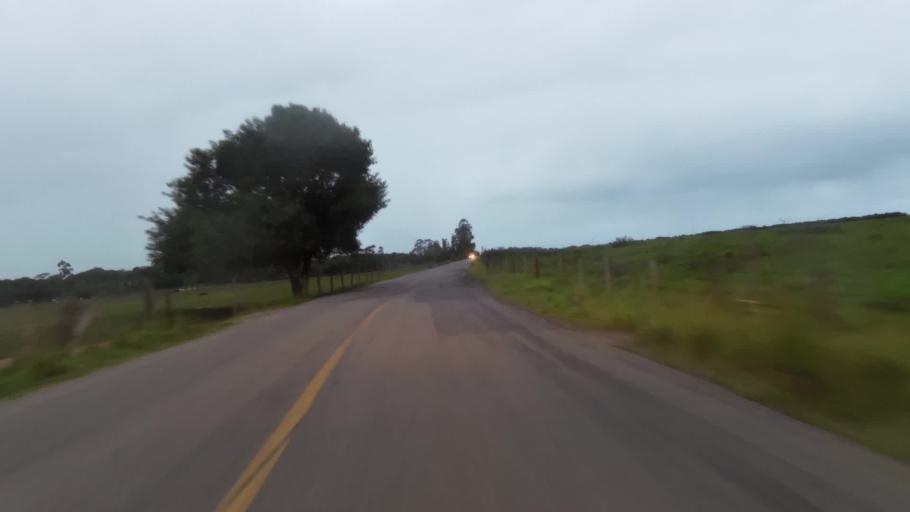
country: BR
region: Espirito Santo
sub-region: Itapemirim
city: Itapemirim
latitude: -20.9797
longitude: -40.8215
